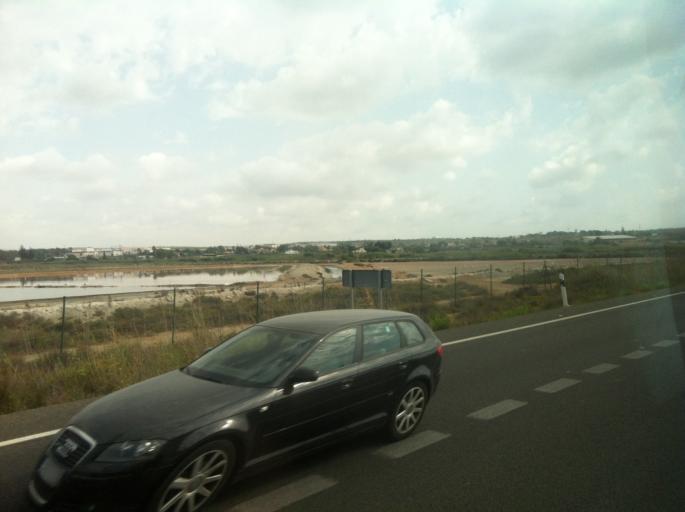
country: ES
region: Valencia
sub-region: Provincia de Alicante
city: Santa Pola
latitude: 38.1964
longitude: -0.5807
